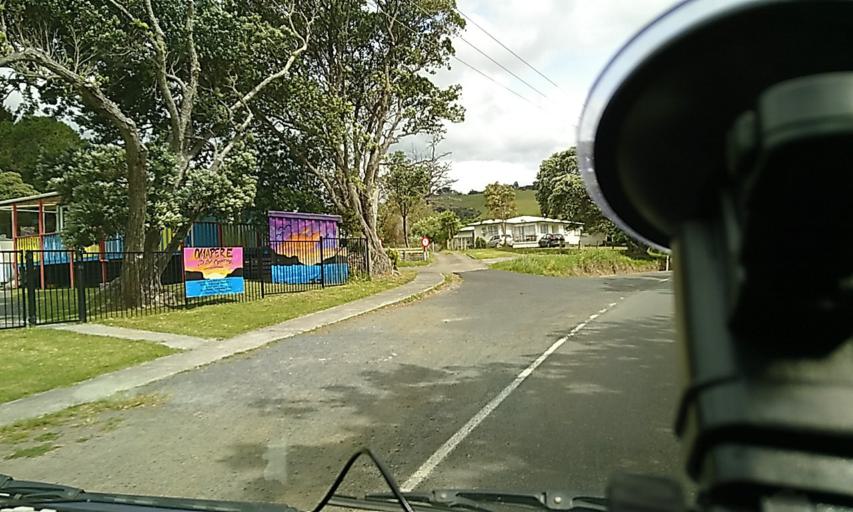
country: NZ
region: Northland
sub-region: Far North District
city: Ahipara
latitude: -35.5247
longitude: 173.3899
